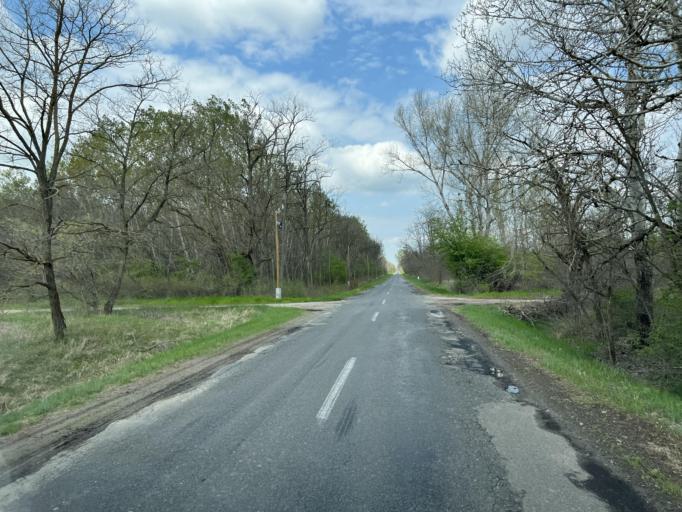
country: HU
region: Pest
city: Orkeny
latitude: 47.0601
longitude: 19.4050
